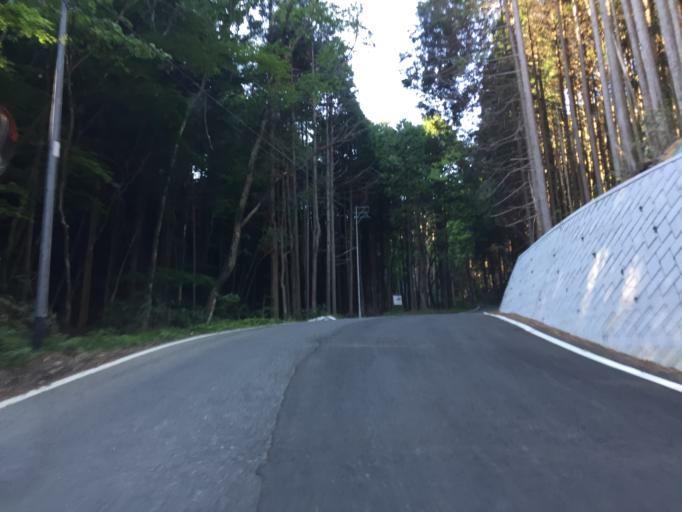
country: JP
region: Ibaraki
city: Kitaibaraki
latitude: 36.8976
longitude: 140.6198
